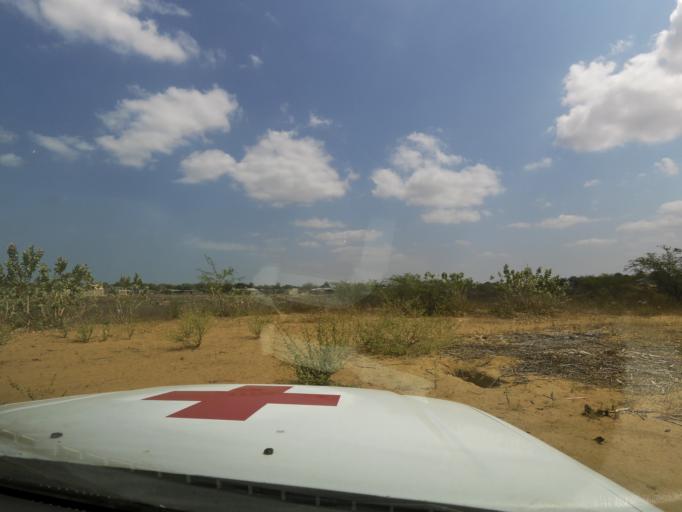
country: CO
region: La Guajira
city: Riohacha
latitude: 11.5204
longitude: -72.9162
